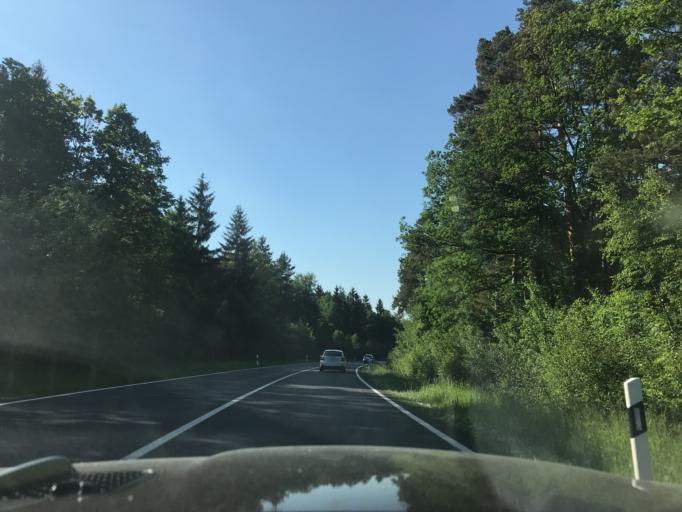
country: DE
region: Thuringia
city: Luisenthal
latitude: 50.7933
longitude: 10.7512
